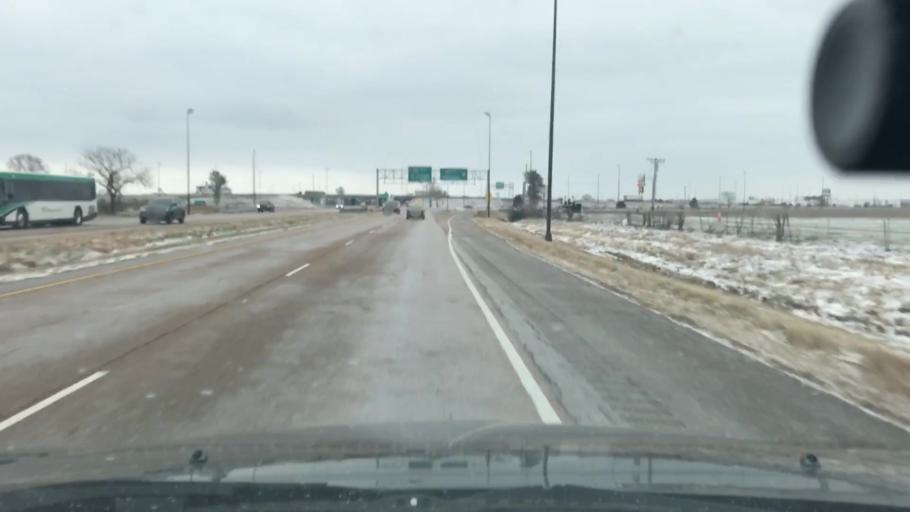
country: US
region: Illinois
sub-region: Madison County
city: Mitchell
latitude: 38.7533
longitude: -90.0690
